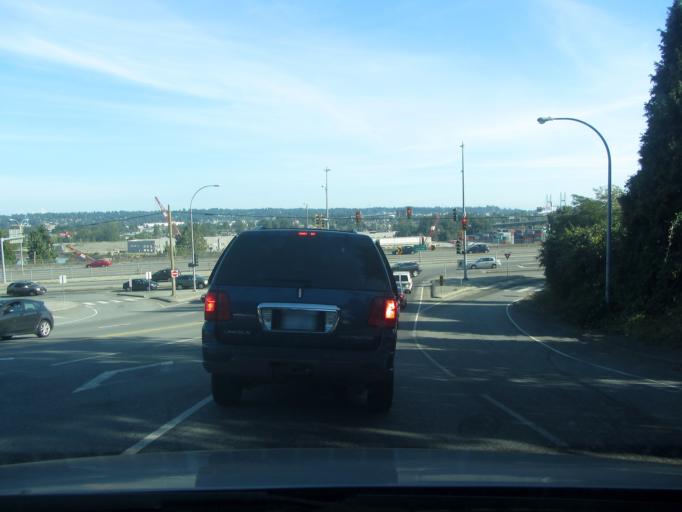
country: CA
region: British Columbia
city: New Westminster
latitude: 49.2006
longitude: -122.9457
